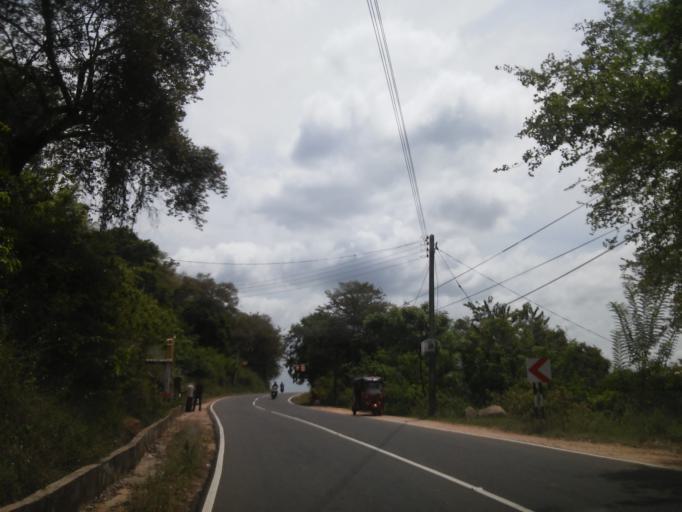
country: LK
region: Eastern Province
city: Trincomalee
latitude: 8.3530
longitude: 80.9830
